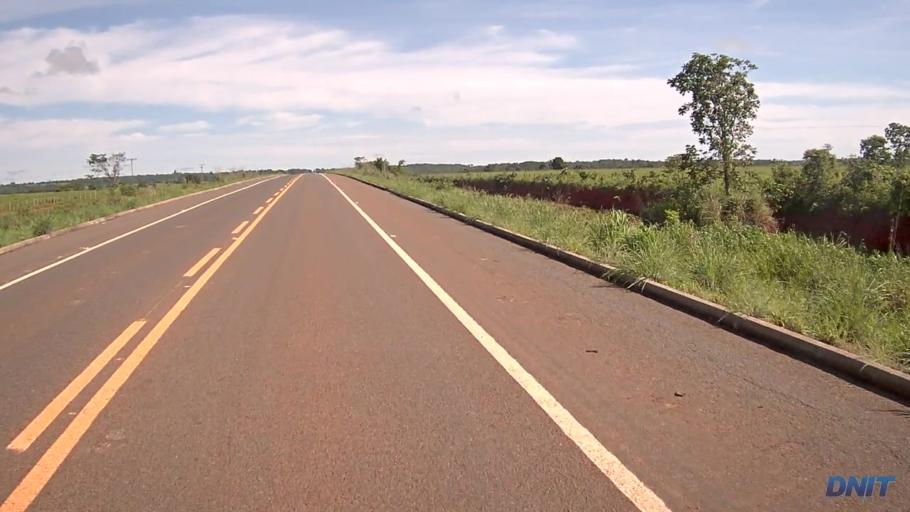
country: BR
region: Goias
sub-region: Sao Miguel Do Araguaia
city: Sao Miguel do Araguaia
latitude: -13.3595
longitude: -50.1469
